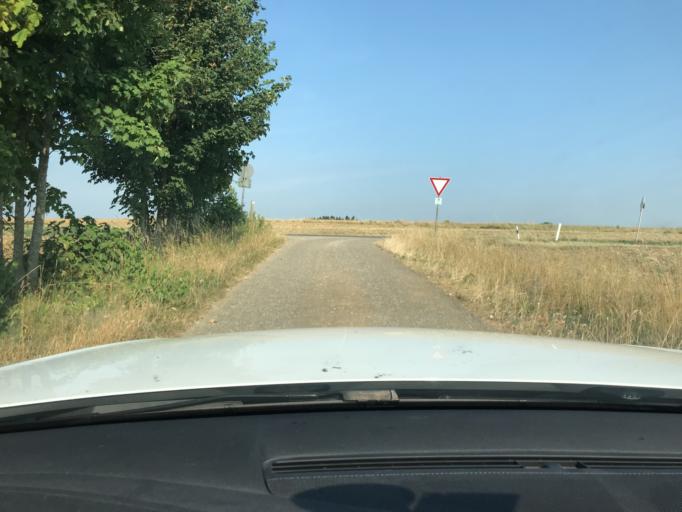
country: DE
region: Bavaria
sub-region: Upper Franconia
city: Pegnitz
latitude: 49.7659
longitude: 11.5953
